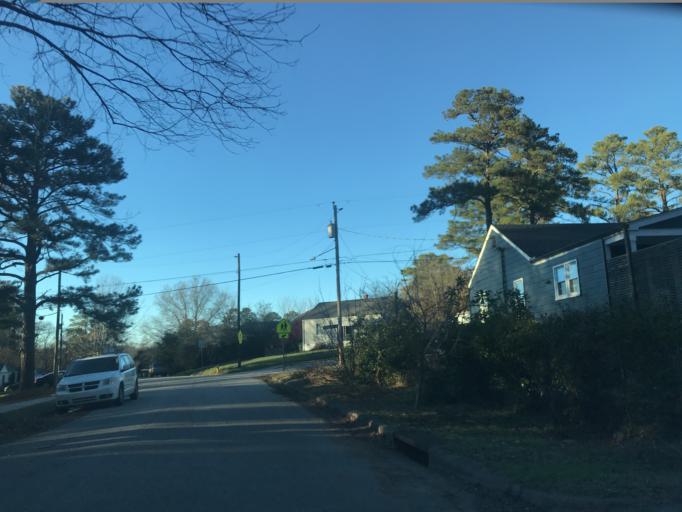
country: US
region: North Carolina
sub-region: Wake County
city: Raleigh
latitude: 35.7973
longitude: -78.6213
